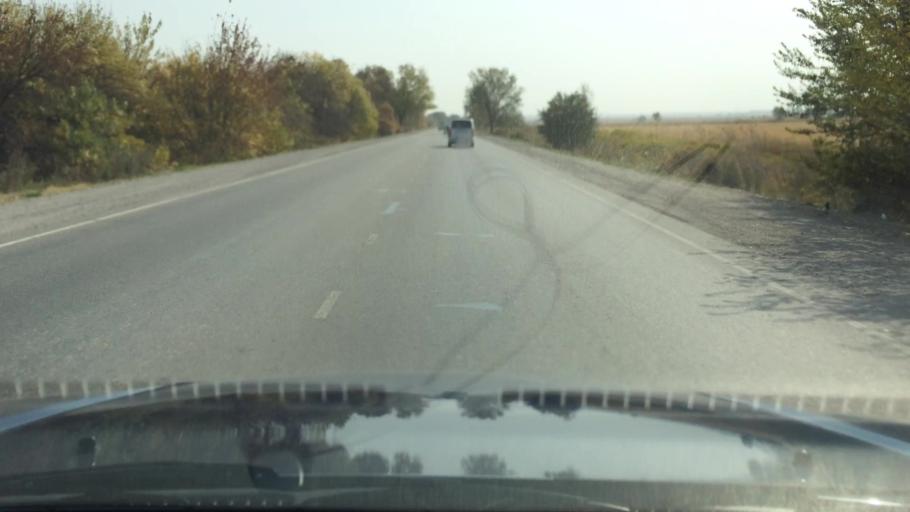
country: KG
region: Chuy
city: Lebedinovka
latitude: 42.9283
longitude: 74.6953
